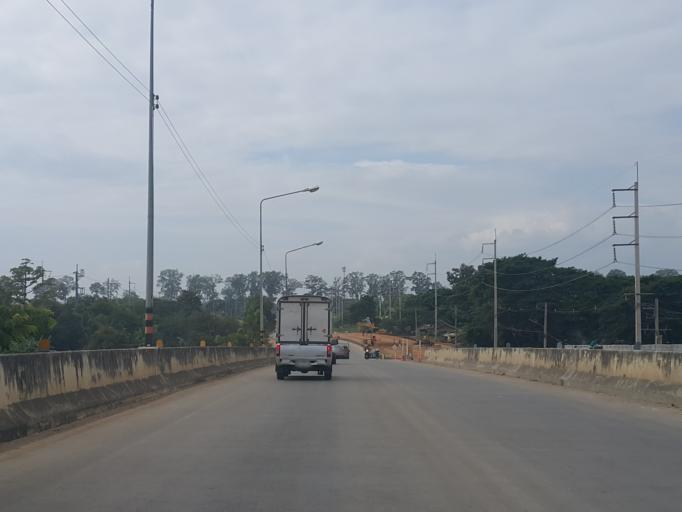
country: TH
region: Chiang Mai
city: Saraphi
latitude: 18.7329
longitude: 99.0309
